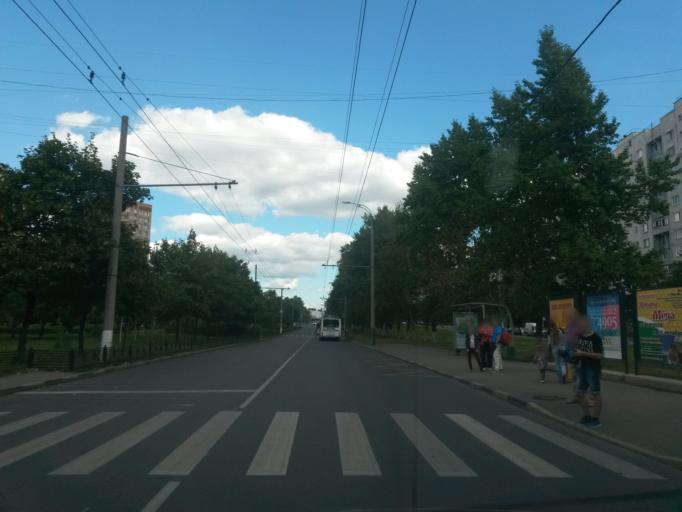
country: RU
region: Moscow
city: Mar'ino
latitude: 55.6505
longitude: 37.7174
